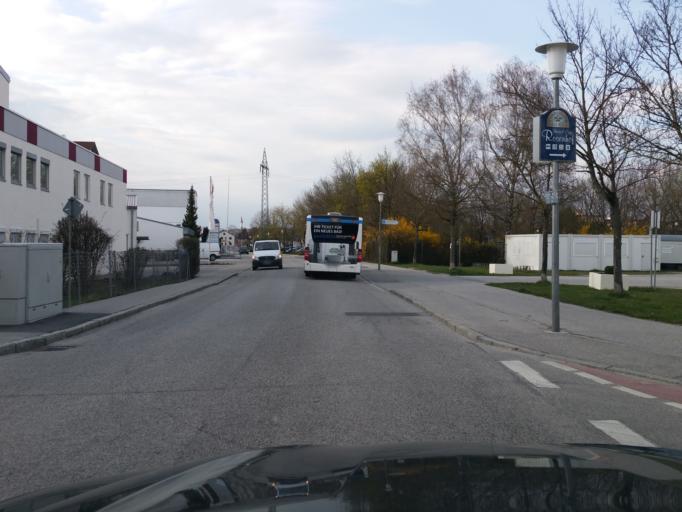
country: DE
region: Bavaria
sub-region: Lower Bavaria
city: Ergolding
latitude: 48.5624
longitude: 12.1675
